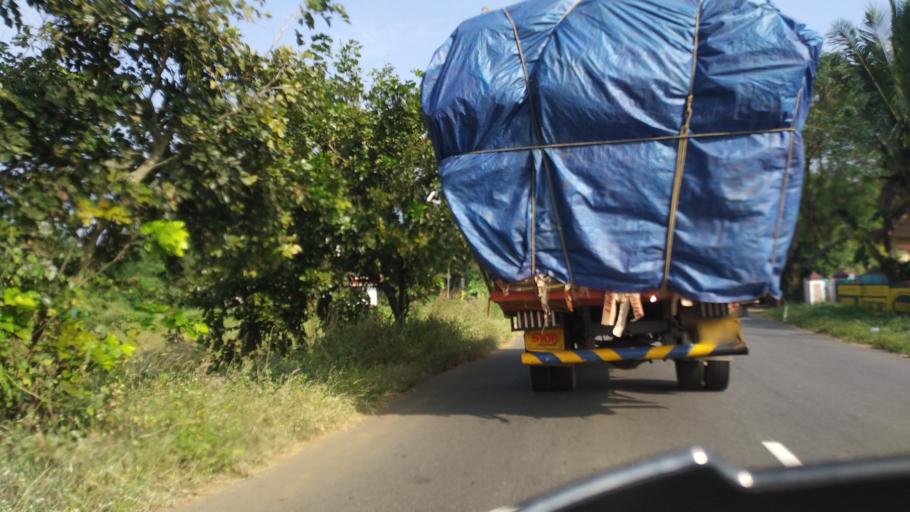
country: IN
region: Kerala
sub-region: Palakkad district
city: Palakkad
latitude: 10.6011
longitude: 76.5494
